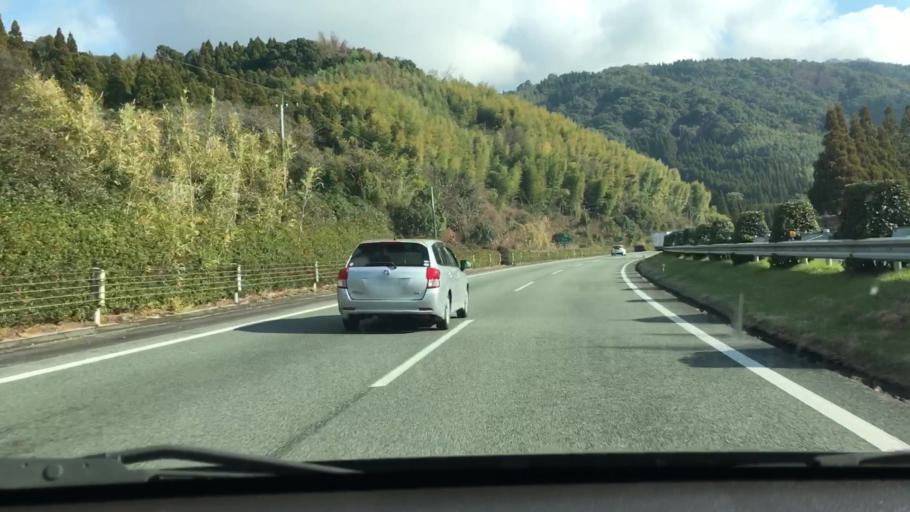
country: JP
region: Kumamoto
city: Matsubase
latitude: 32.6167
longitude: 130.7208
